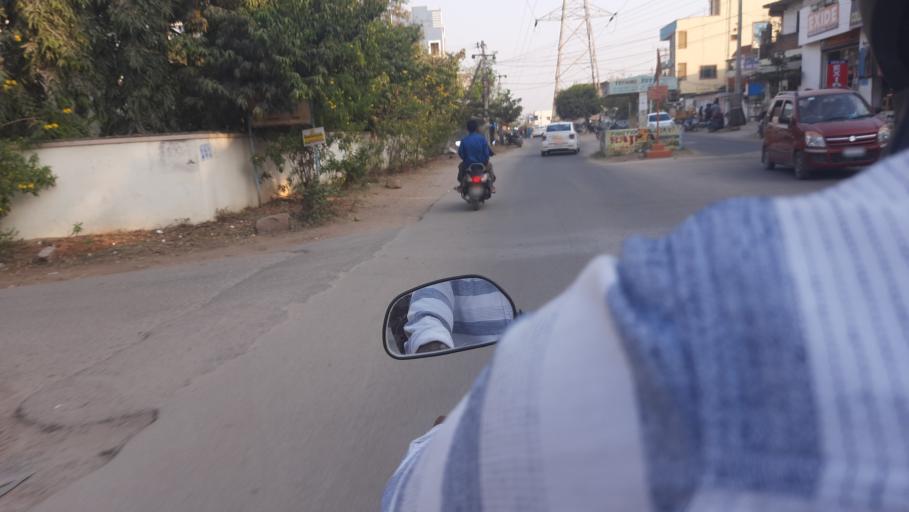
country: IN
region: Telangana
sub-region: Rangareddi
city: Secunderabad
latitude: 17.4916
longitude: 78.5481
